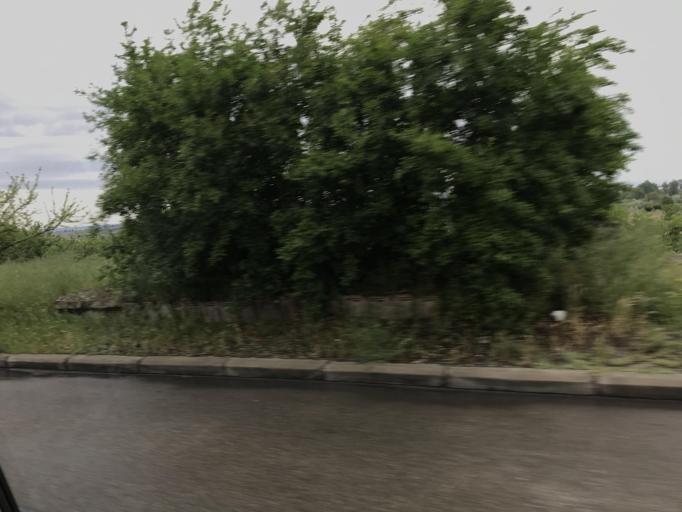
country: GE
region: Kvemo Kartli
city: Rust'avi
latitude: 41.5539
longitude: 44.9912
